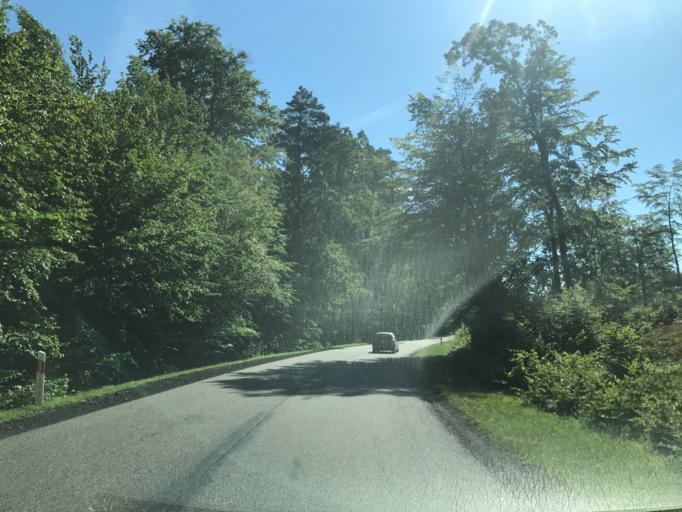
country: PL
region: Pomeranian Voivodeship
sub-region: Powiat slupski
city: Potegowo
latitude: 54.4097
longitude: 17.4359
